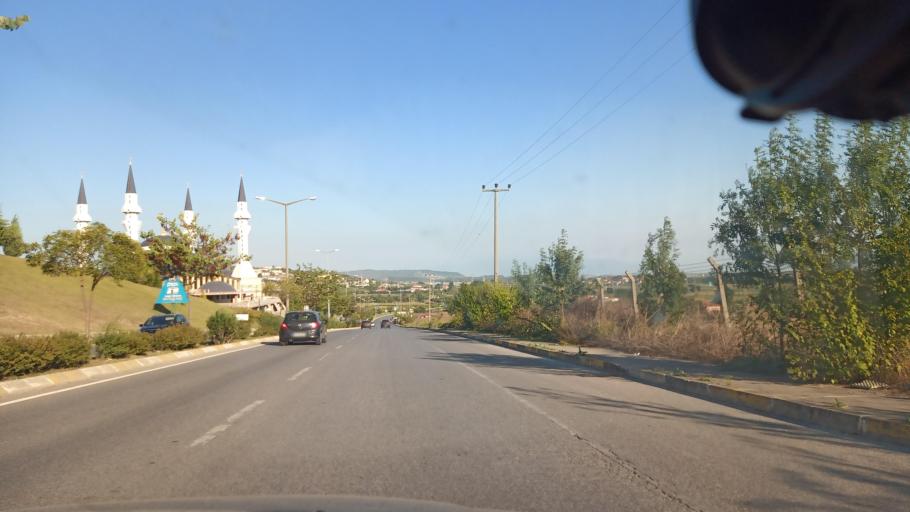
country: TR
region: Sakarya
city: Kazimpasa
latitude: 40.8520
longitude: 30.3104
